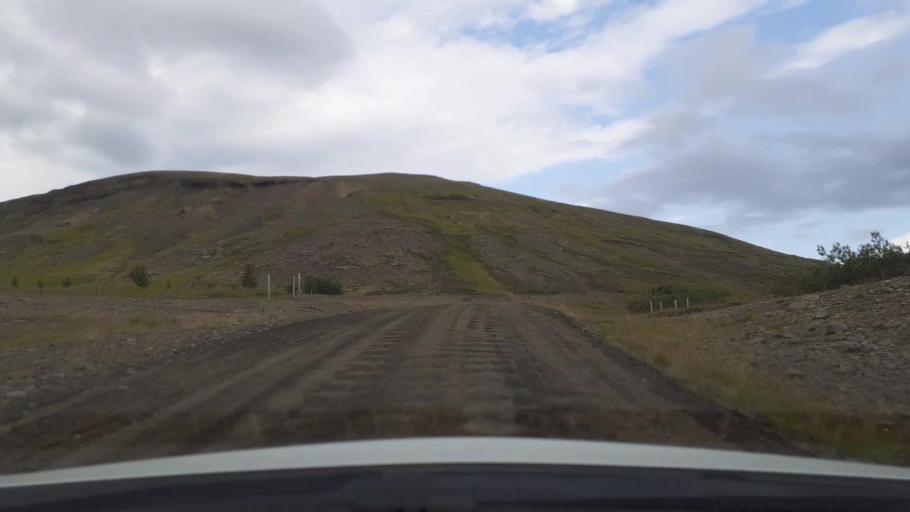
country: IS
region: Capital Region
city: Mosfellsbaer
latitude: 64.2951
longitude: -21.6620
